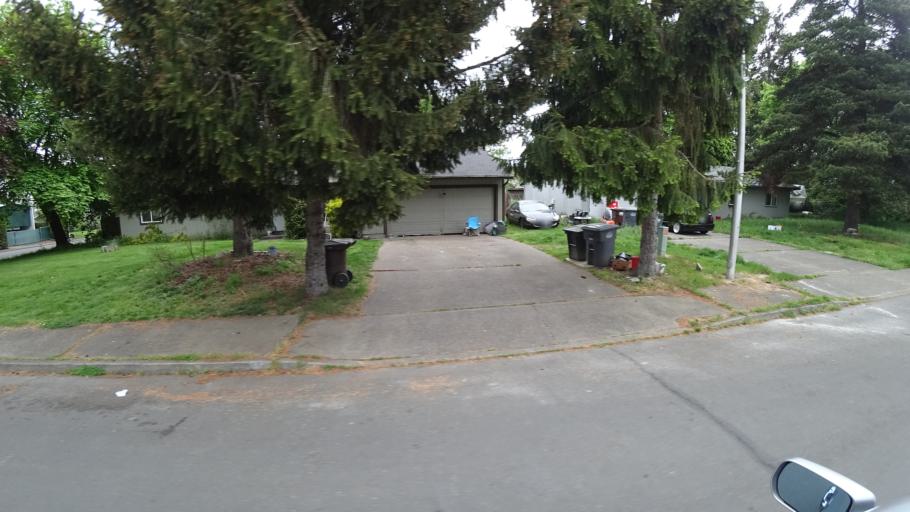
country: US
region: Oregon
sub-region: Washington County
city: Hillsboro
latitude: 45.5359
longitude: -122.9727
